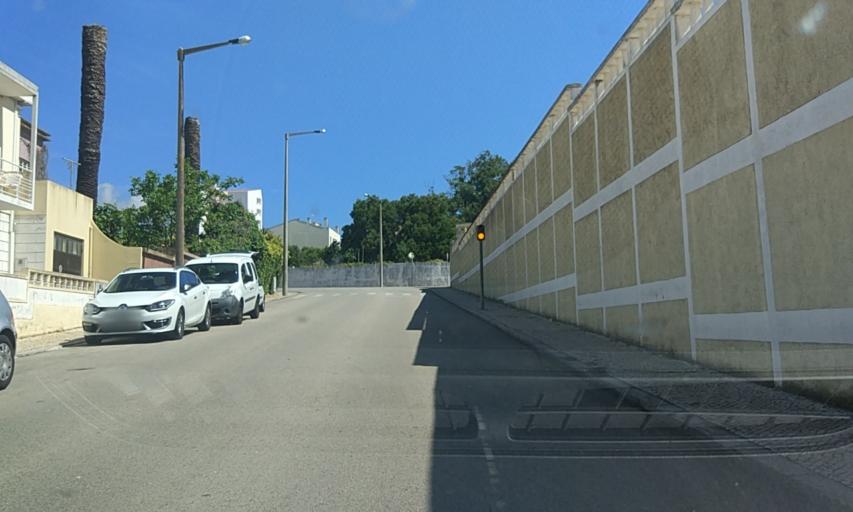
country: PT
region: Coimbra
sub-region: Figueira da Foz
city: Figueira da Foz
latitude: 40.1538
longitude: -8.8526
